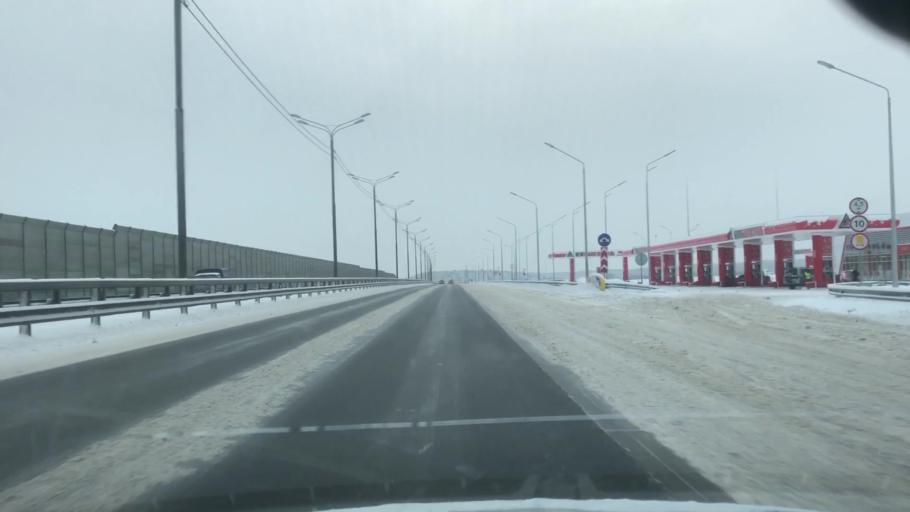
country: RU
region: Moskovskaya
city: Barybino
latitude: 55.1938
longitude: 37.8929
